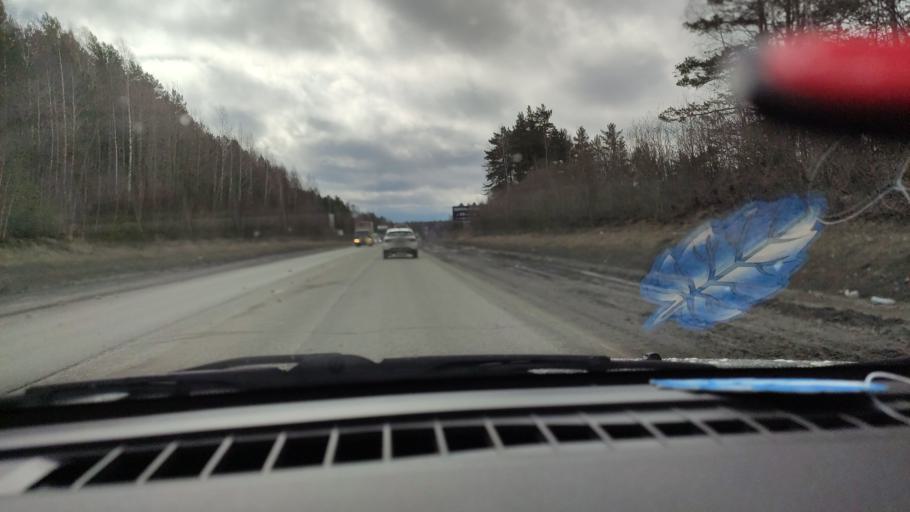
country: RU
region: Sverdlovsk
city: Talitsa
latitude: 56.8681
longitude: 60.0438
